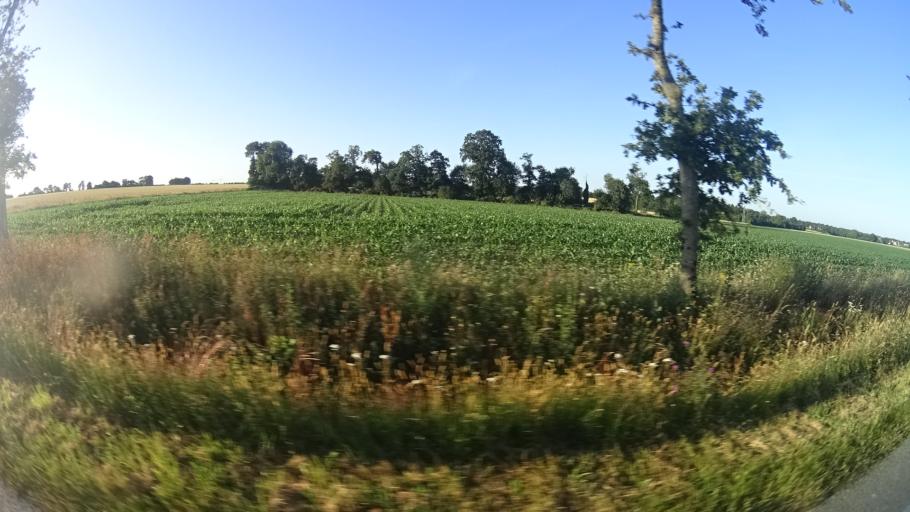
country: FR
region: Brittany
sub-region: Departement d'Ille-et-Vilaine
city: Grand-Fougeray
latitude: 47.7289
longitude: -1.7545
